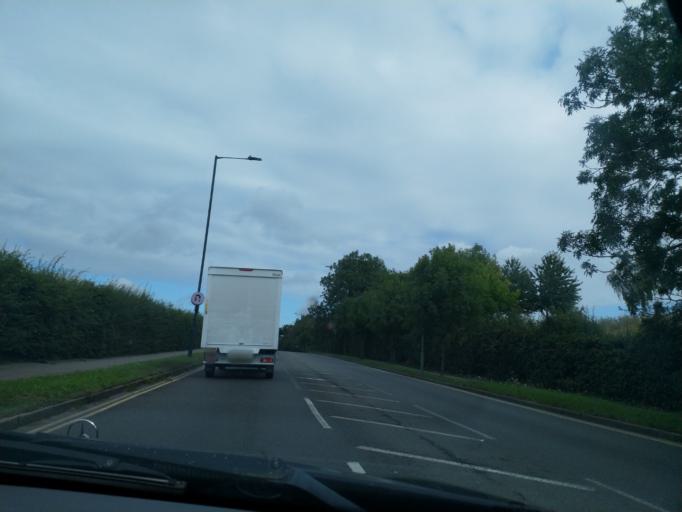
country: GB
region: England
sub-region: Greater London
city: Harrow on the Hill
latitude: 51.5717
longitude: -0.3237
